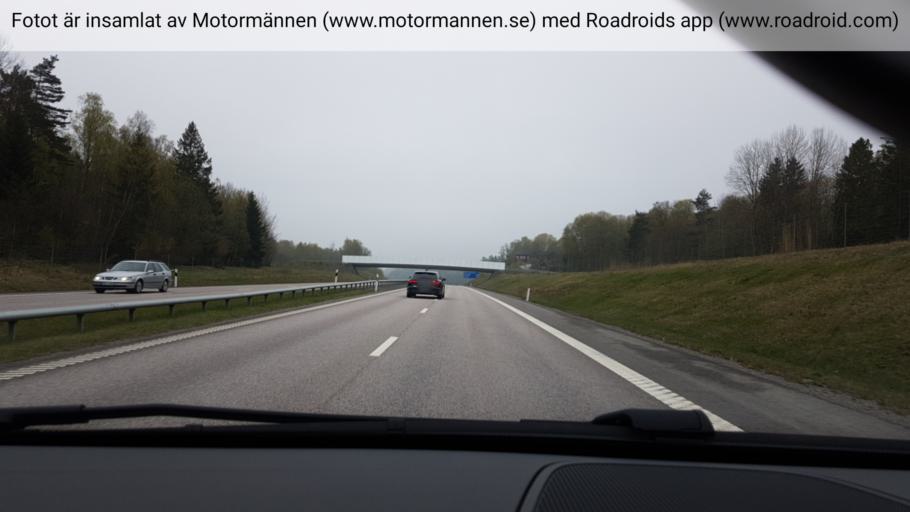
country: SE
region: Stockholm
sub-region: Nynashamns Kommun
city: Osmo
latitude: 58.9848
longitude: 17.9193
